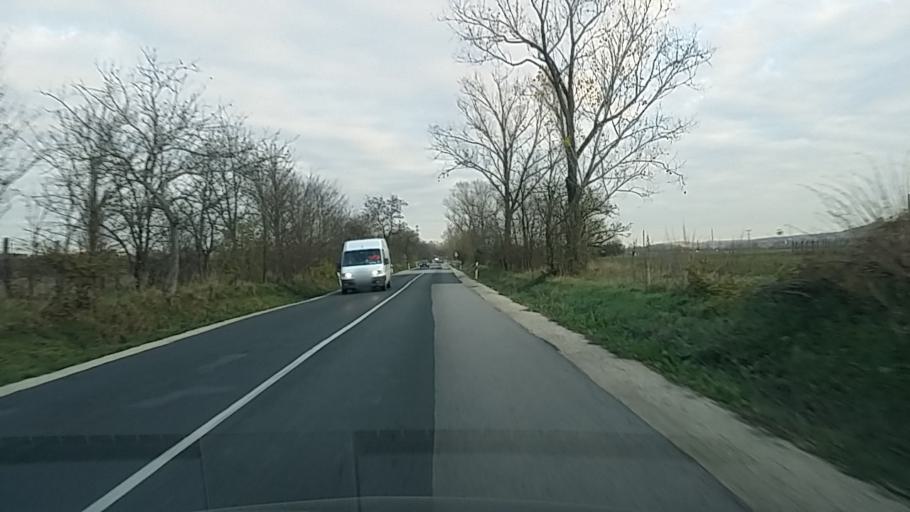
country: HU
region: Pest
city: Vac
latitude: 47.7703
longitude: 19.1678
